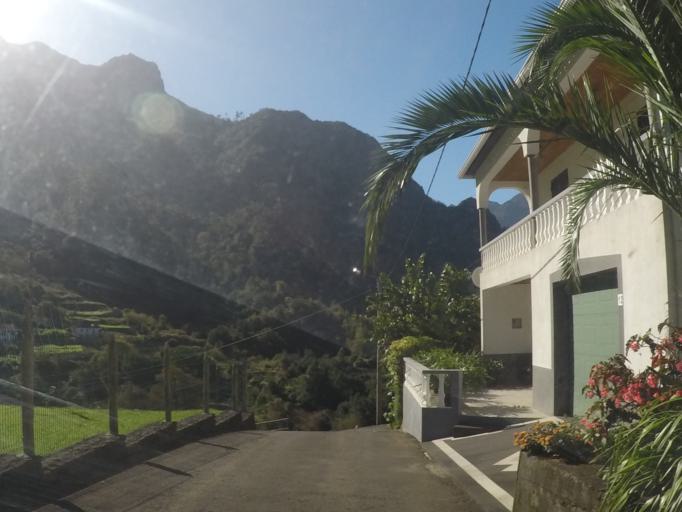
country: PT
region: Madeira
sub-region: Santana
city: Santana
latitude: 32.8003
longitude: -16.9608
